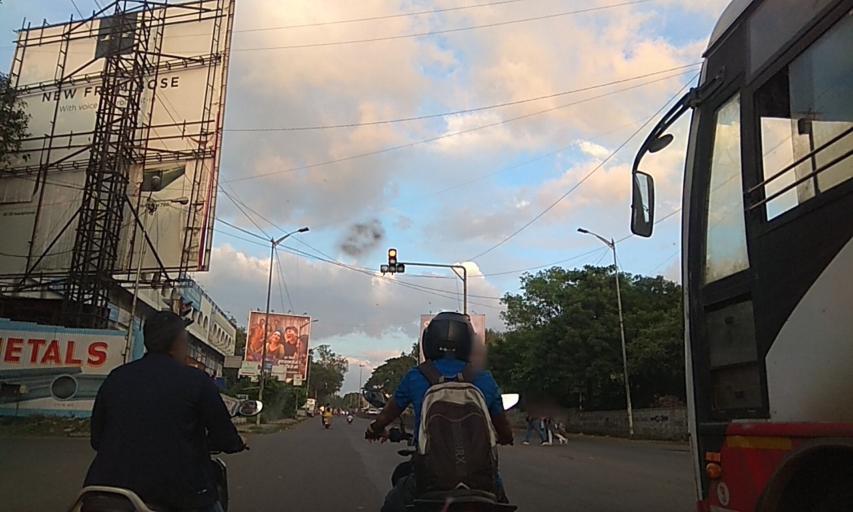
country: IN
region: Maharashtra
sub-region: Pune Division
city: Pune
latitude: 18.5022
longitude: 73.8748
